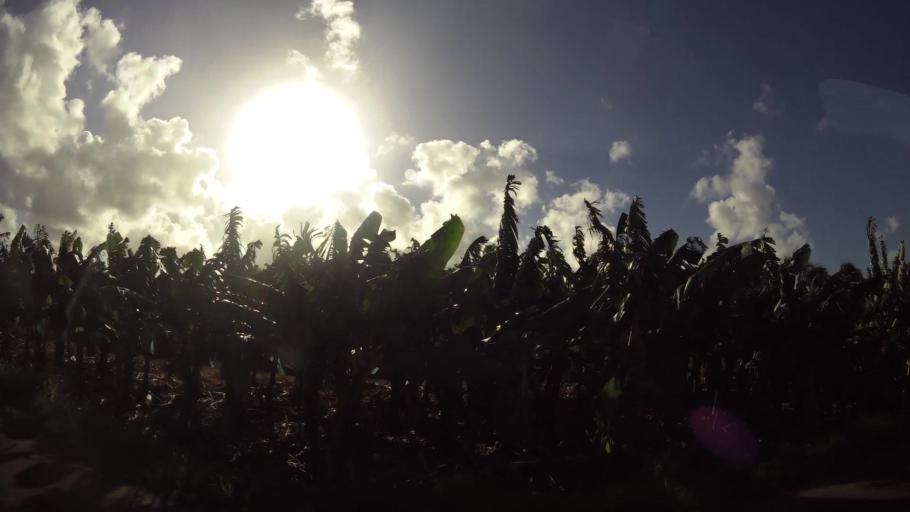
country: MQ
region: Martinique
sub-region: Martinique
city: Ducos
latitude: 14.5965
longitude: -60.9789
